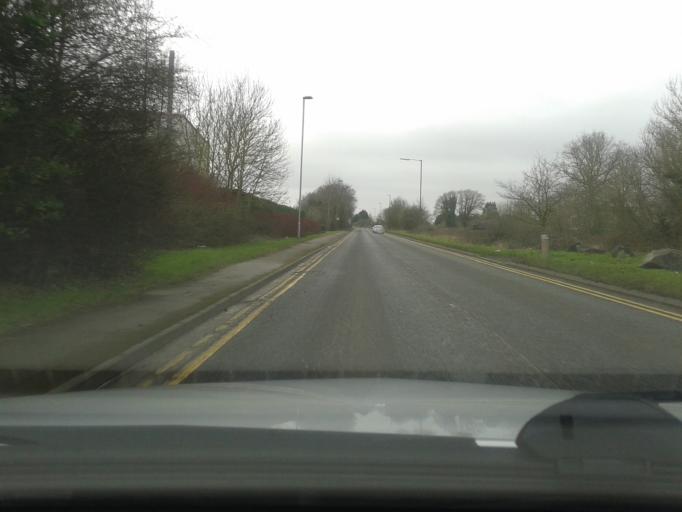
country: GB
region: England
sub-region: South Gloucestershire
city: Yate
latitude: 51.5481
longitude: -2.4381
